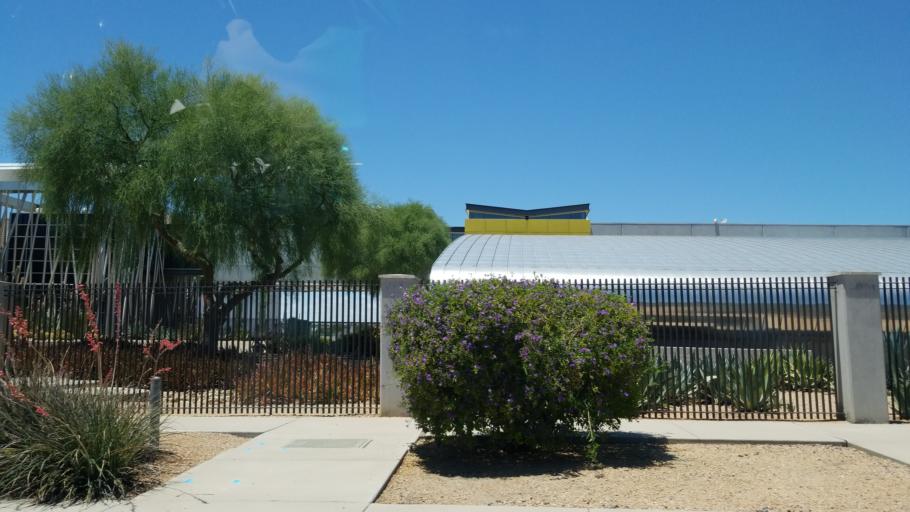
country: US
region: Arizona
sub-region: Maricopa County
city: Paradise Valley
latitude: 33.6241
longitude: -111.9053
